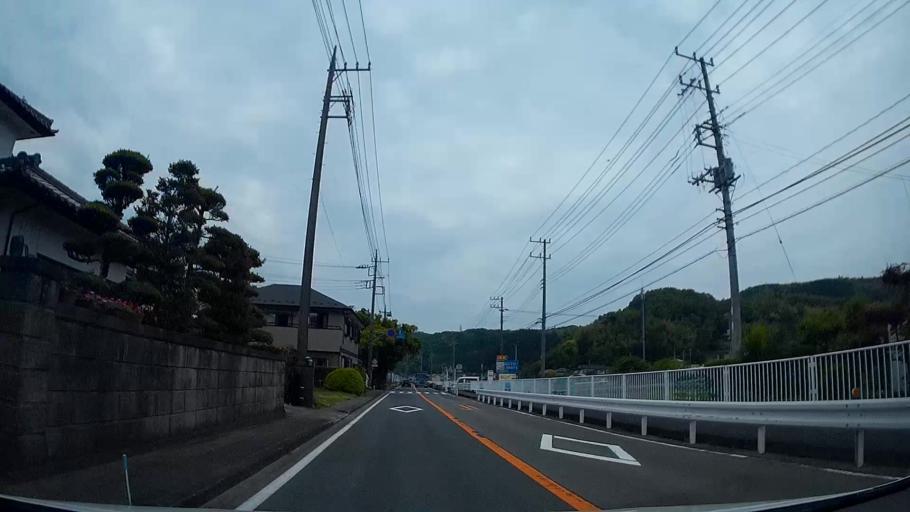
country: JP
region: Shizuoka
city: Ito
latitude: 34.9595
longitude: 138.9963
